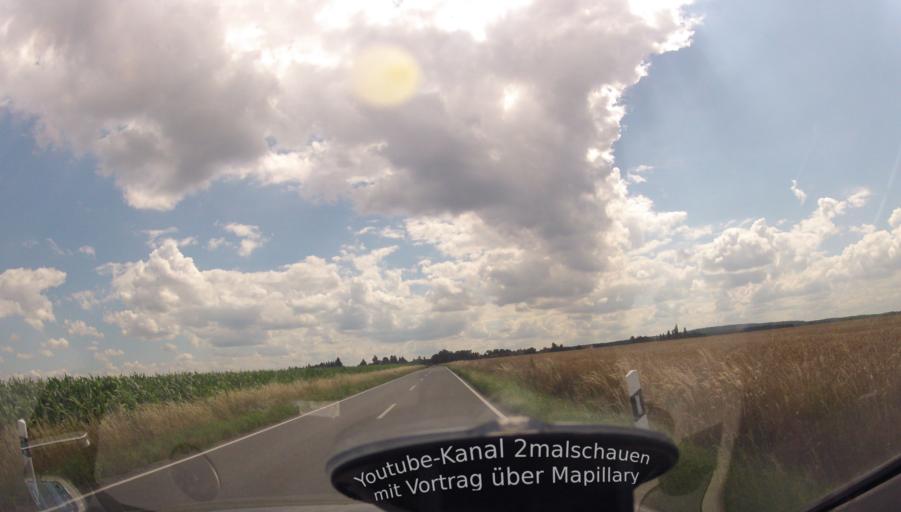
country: DE
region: Saxony
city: Schildau
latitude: 51.4657
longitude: 12.9366
